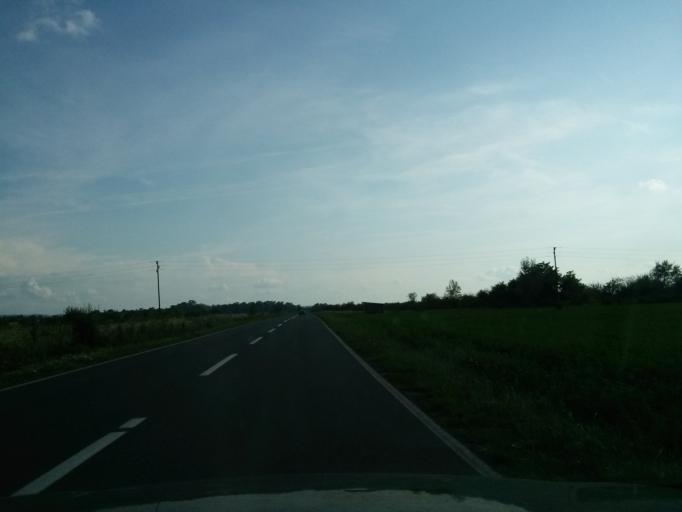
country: HR
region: Grad Zagreb
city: Zadvorsko
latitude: 45.7442
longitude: 15.9178
